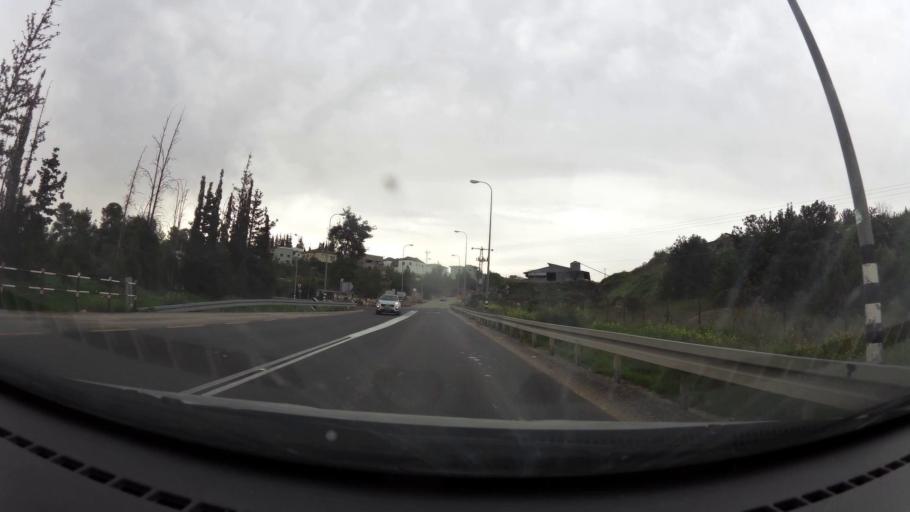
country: PS
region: West Bank
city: Surif
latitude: 31.6744
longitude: 35.0112
